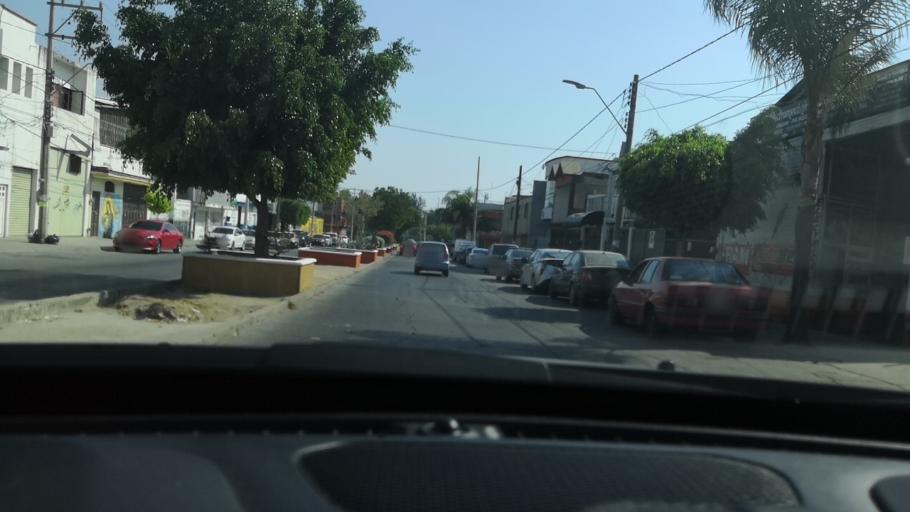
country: MX
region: Guanajuato
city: Leon
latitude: 21.1065
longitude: -101.7028
